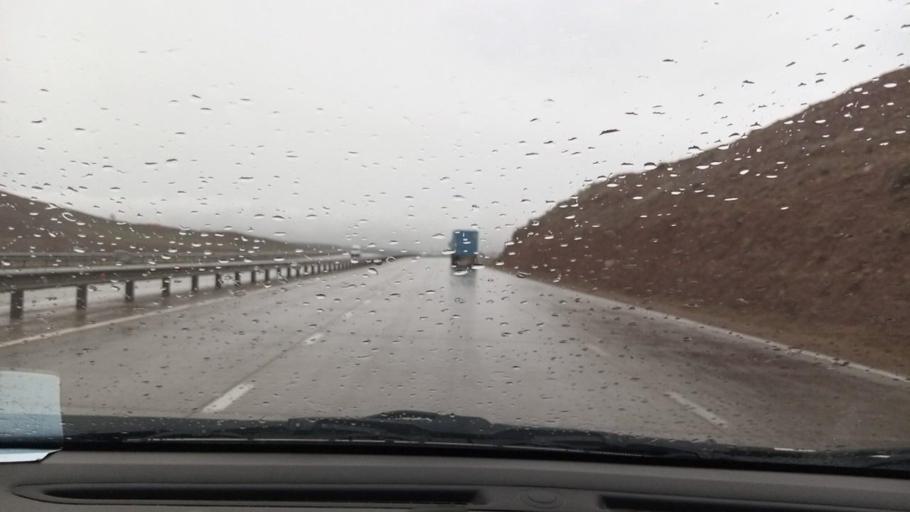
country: UZ
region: Namangan
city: Pop Shahri
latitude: 40.9289
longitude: 70.7120
